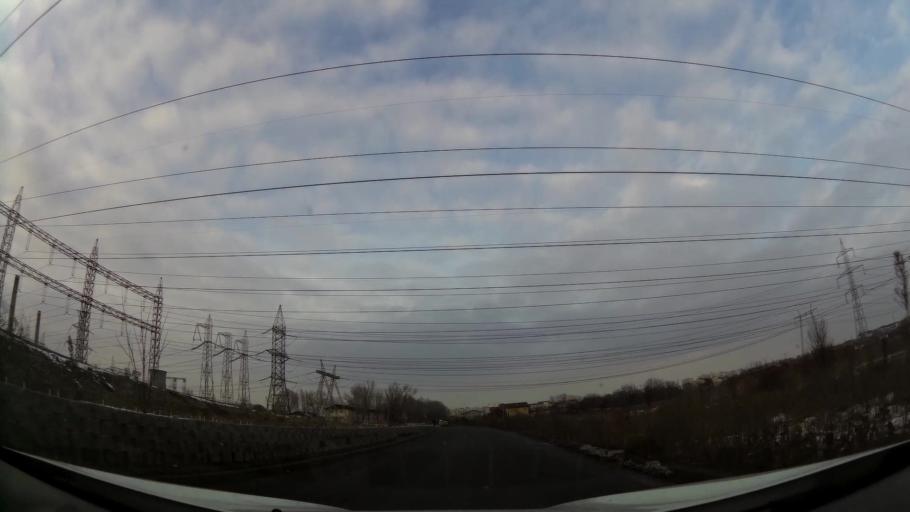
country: RO
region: Ilfov
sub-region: Comuna Popesti-Leordeni
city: Popesti-Leordeni
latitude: 44.4002
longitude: 26.1609
